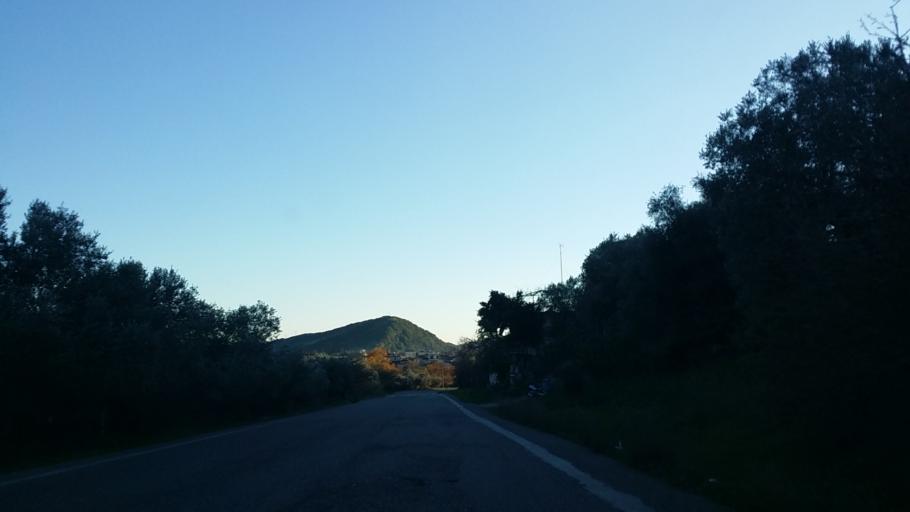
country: GR
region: West Greece
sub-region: Nomos Aitolias kai Akarnanias
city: Lepenou
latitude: 38.7433
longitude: 21.3462
